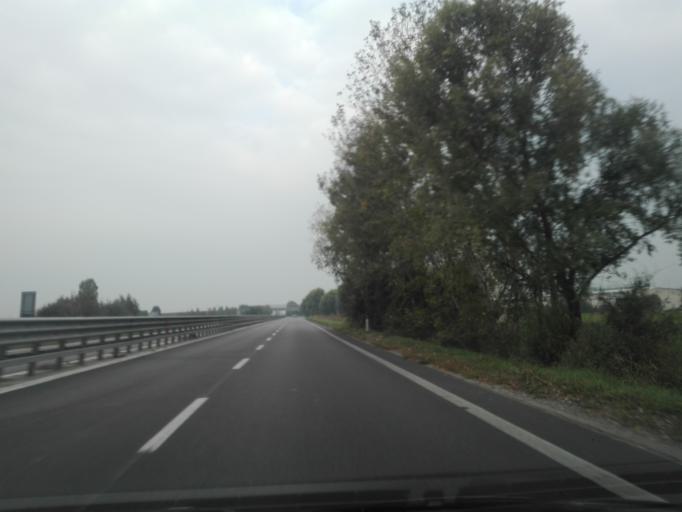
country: IT
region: Veneto
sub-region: Provincia di Verona
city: Villa Bartolomea
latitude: 45.1460
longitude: 11.3479
